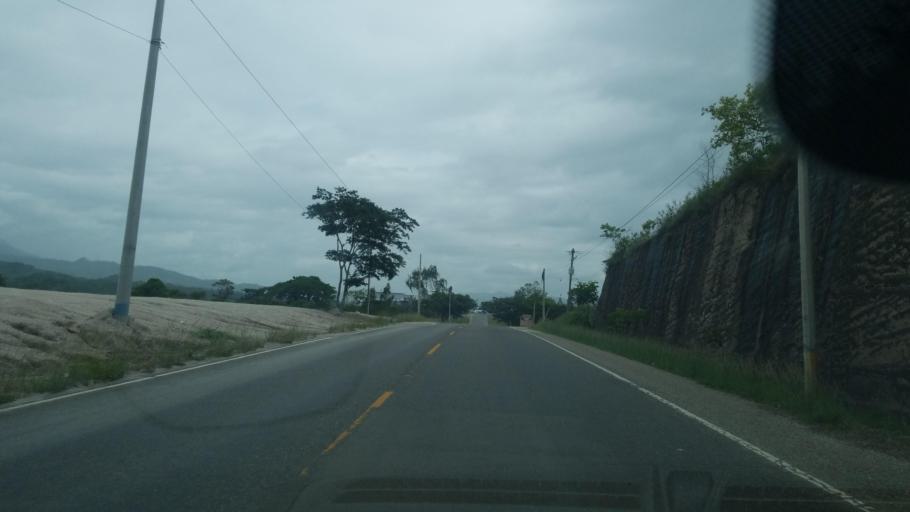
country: HN
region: Ocotepeque
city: Lucerna
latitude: 14.5458
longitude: -88.9459
